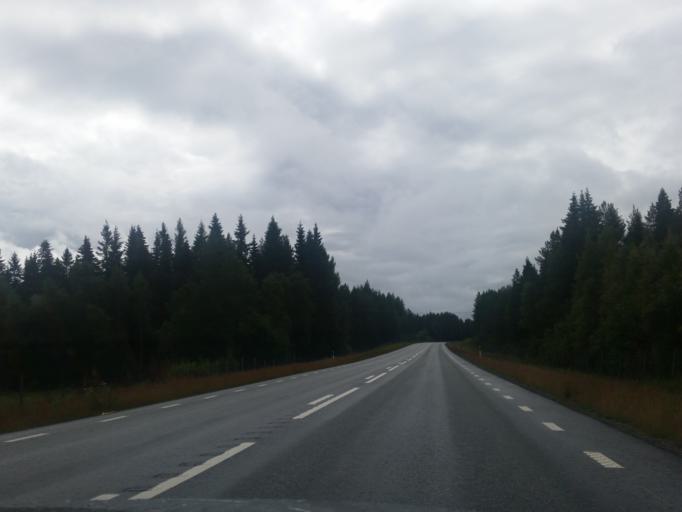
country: SE
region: Vaesterbotten
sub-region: Robertsfors Kommun
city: Robertsfors
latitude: 64.0281
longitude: 20.8413
